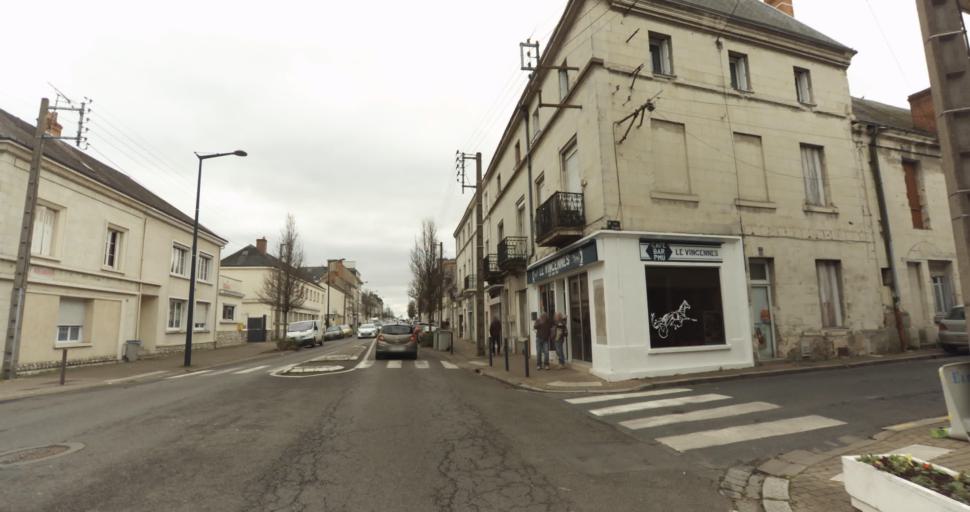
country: FR
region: Pays de la Loire
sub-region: Departement de Maine-et-Loire
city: Saumur
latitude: 47.2697
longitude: -0.0670
